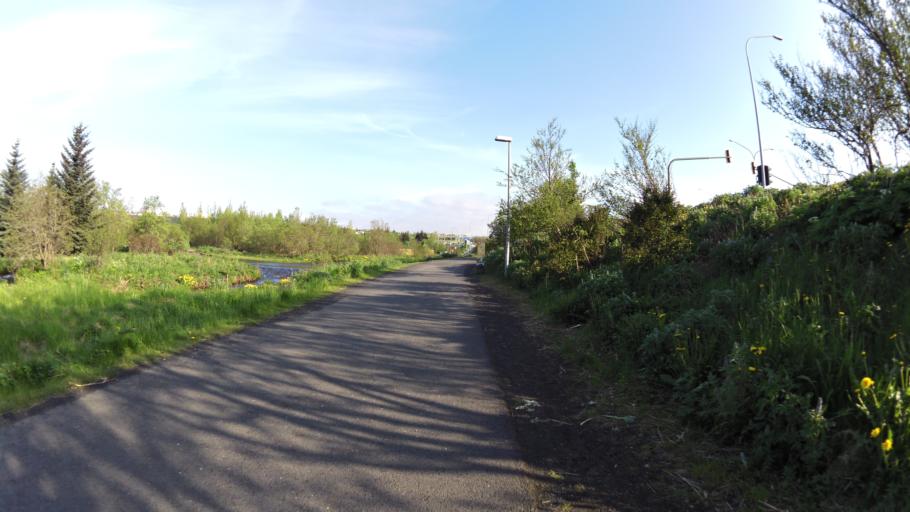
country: IS
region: Capital Region
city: Reykjavik
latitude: 64.1205
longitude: -21.8462
